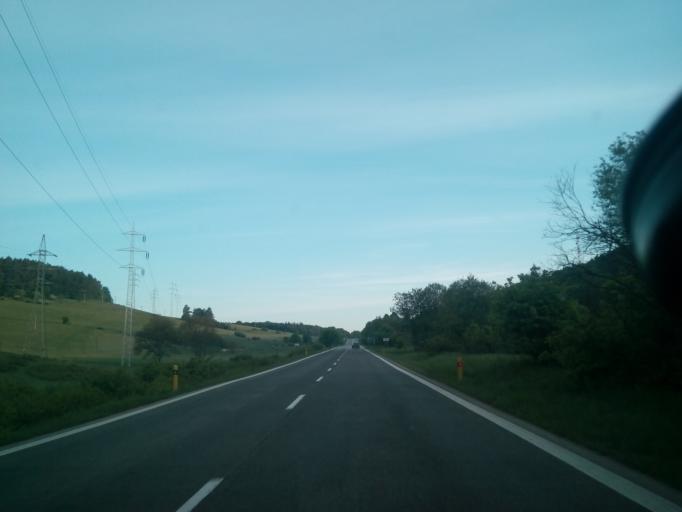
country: SK
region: Kosicky
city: Roznava
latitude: 48.6137
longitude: 20.6342
